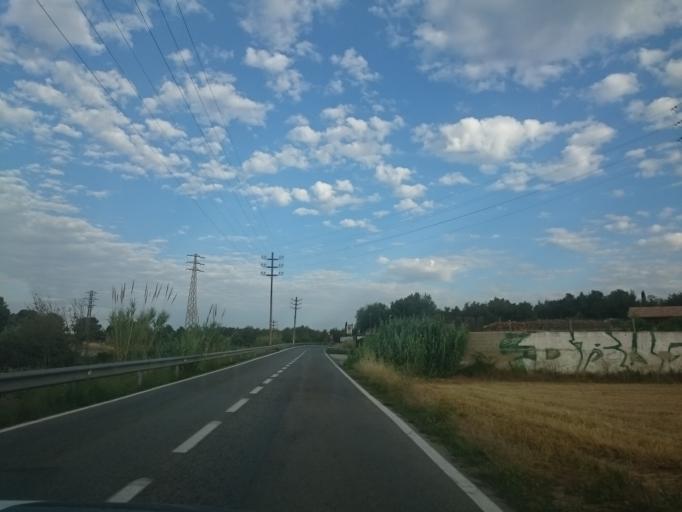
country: ES
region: Catalonia
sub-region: Provincia de Barcelona
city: Vilanova i la Geltru
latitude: 41.2300
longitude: 1.6954
